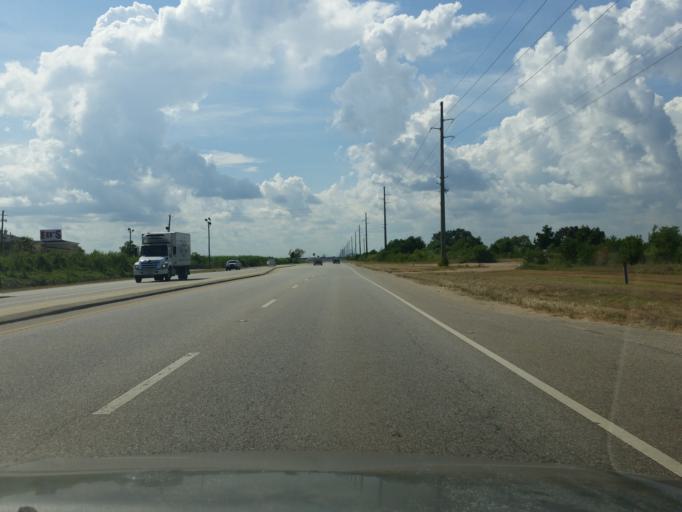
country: US
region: Alabama
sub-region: Baldwin County
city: Spanish Fort
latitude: 30.6744
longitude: -87.9634
